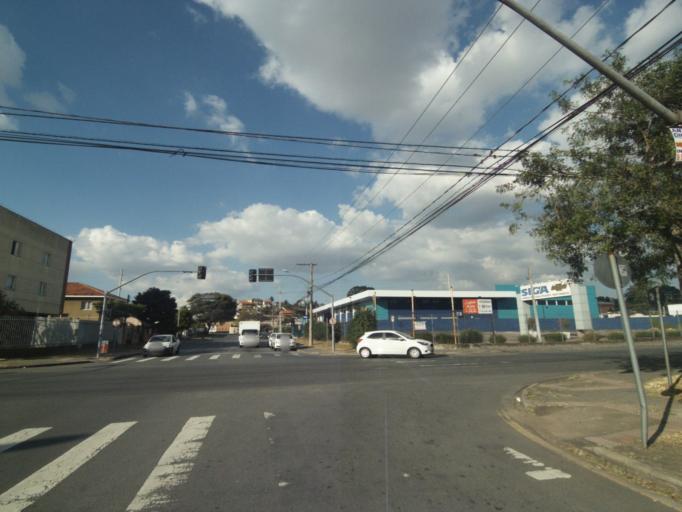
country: BR
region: Parana
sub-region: Curitiba
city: Curitiba
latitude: -25.4579
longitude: -49.2515
